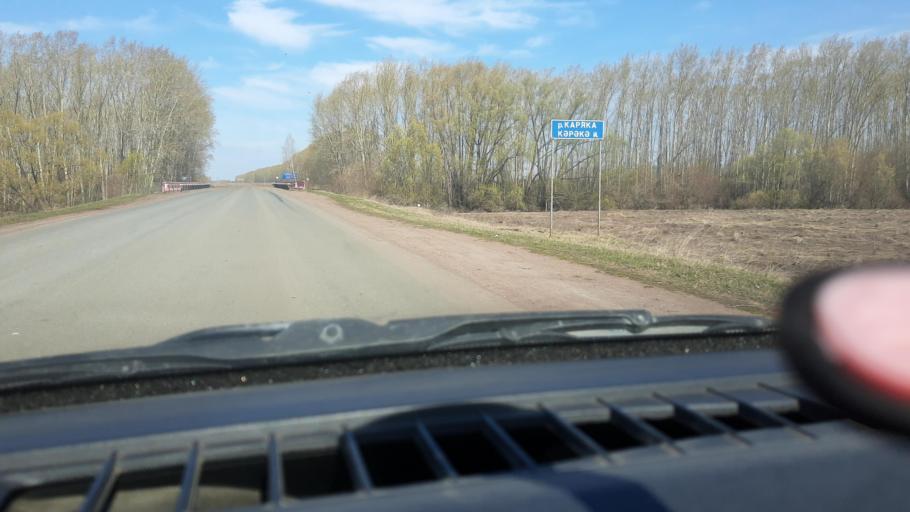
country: RU
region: Bashkortostan
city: Asanovo
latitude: 54.9697
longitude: 55.5399
